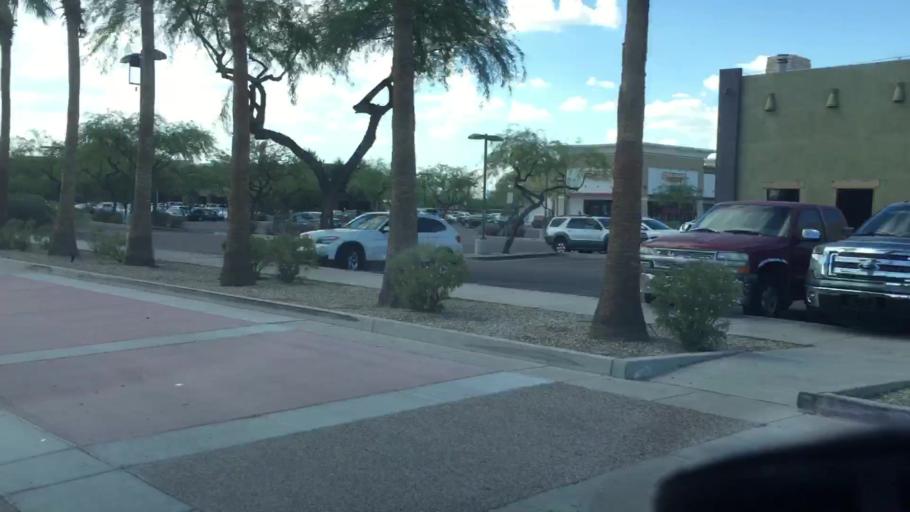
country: US
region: Arizona
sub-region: Maricopa County
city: Gilbert
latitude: 33.3840
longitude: -111.8061
